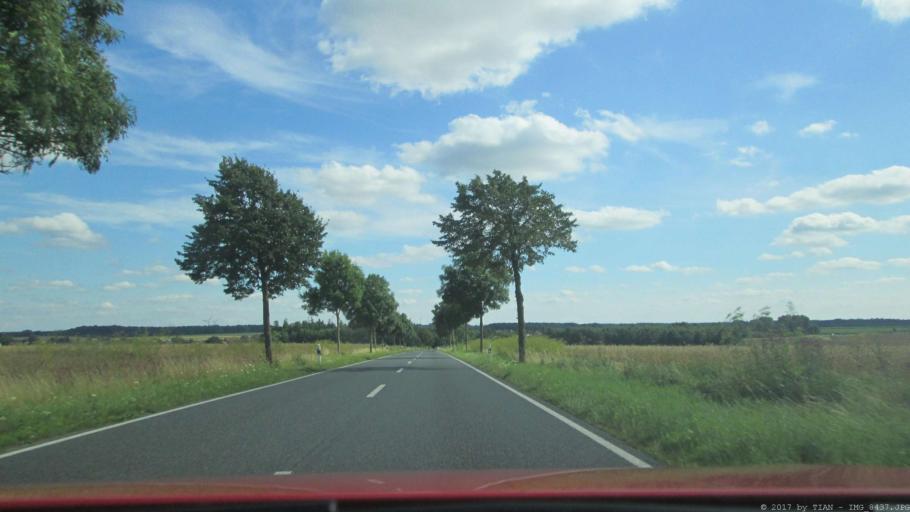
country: DE
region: Lower Saxony
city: Danndorf
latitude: 52.4017
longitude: 10.8491
